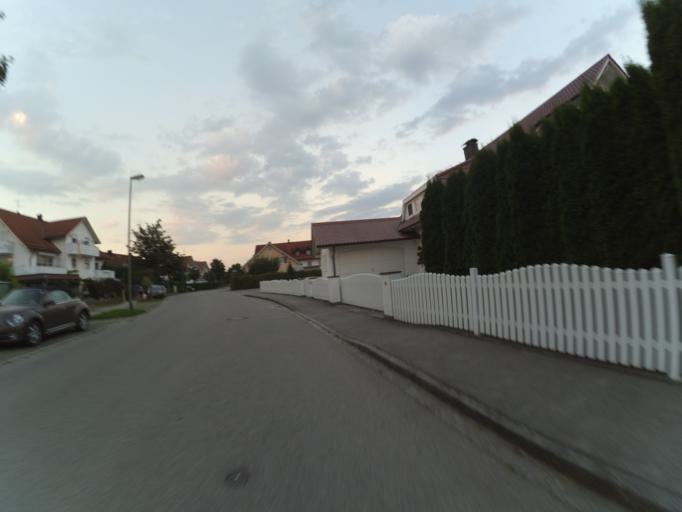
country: DE
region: Bavaria
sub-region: Swabia
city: Turkheim
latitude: 48.0582
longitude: 10.6329
